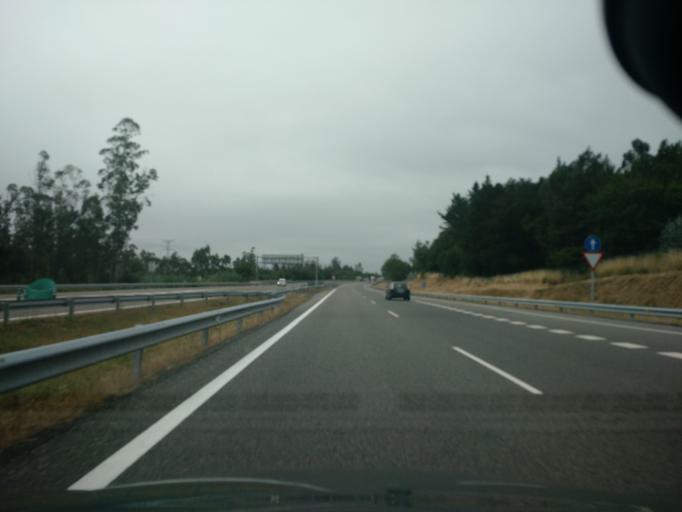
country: ES
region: Galicia
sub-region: Provincia da Coruna
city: Ordes
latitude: 43.0778
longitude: -8.3582
